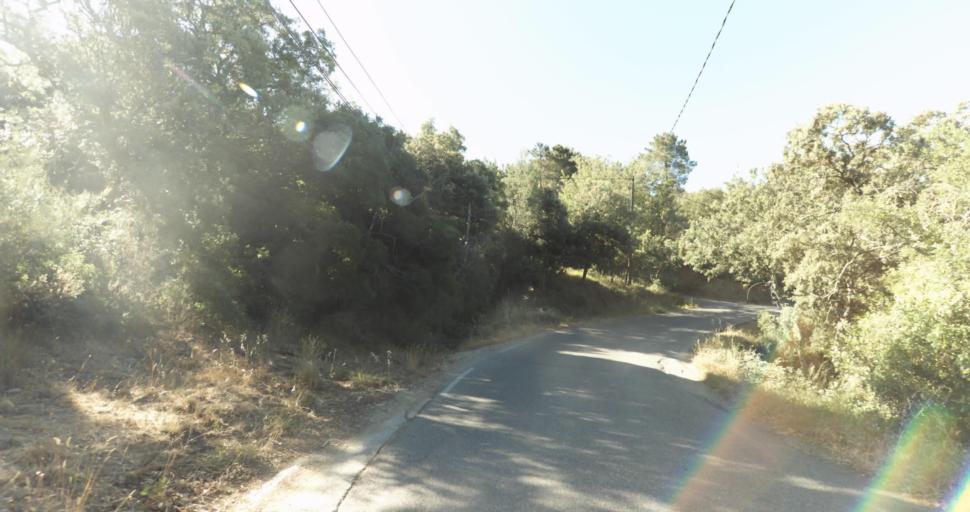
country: FR
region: Provence-Alpes-Cote d'Azur
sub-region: Departement du Var
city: Gassin
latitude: 43.2172
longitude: 6.5854
